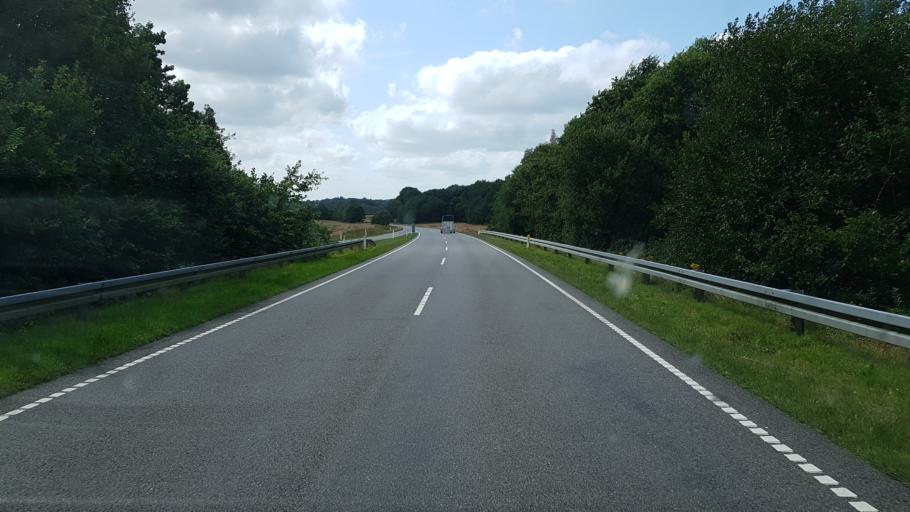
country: DK
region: South Denmark
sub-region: Vejen Kommune
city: Vejen
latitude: 55.5467
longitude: 9.0885
